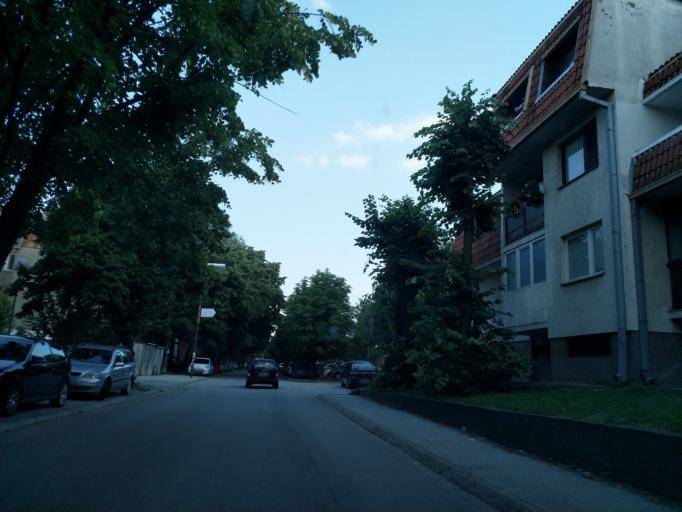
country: RS
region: Central Serbia
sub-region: Pomoravski Okrug
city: Jagodina
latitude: 43.9793
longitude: 21.2469
